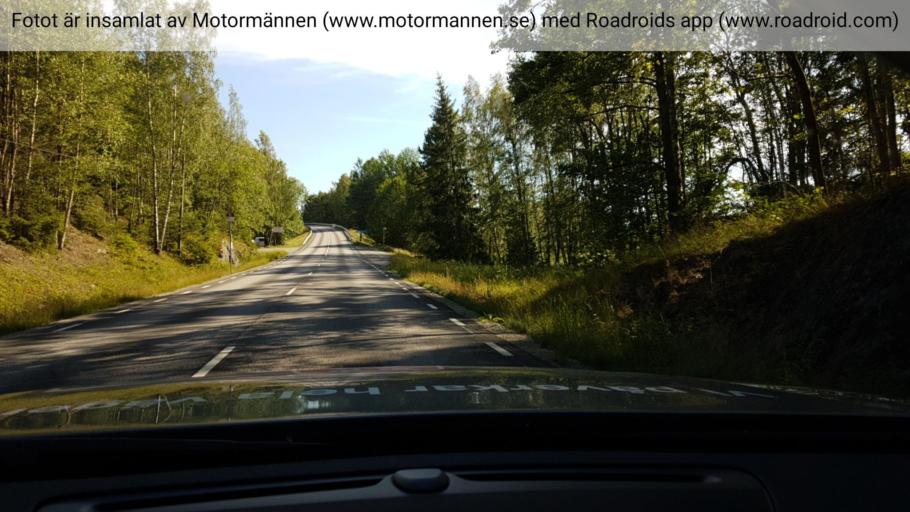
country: SE
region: Stockholm
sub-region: Nynashamns Kommun
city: Nynashamn
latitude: 58.9605
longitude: 17.9620
